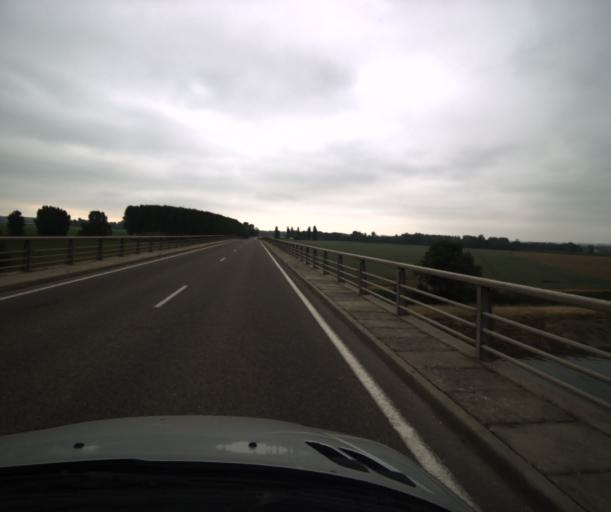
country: FR
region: Midi-Pyrenees
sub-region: Departement du Tarn-et-Garonne
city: Saint-Nicolas-de-la-Grave
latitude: 44.0840
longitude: 0.9873
